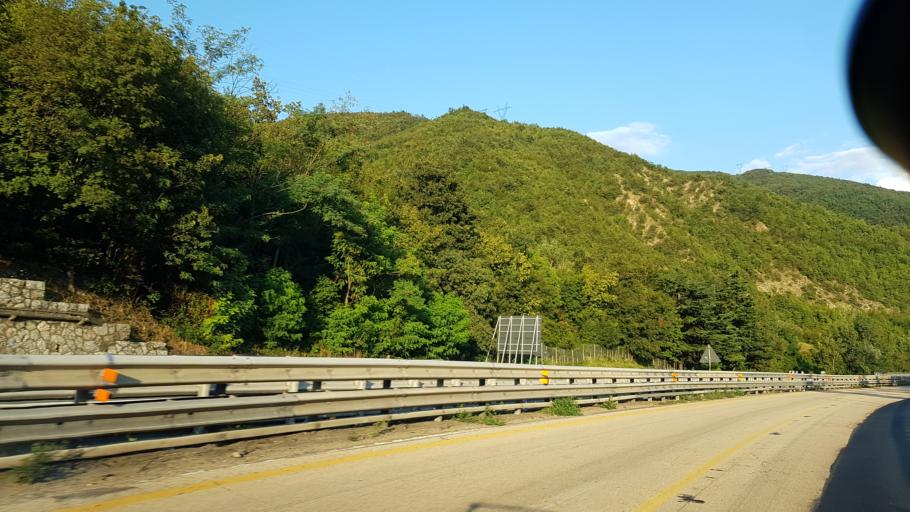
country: IT
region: Liguria
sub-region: Provincia di Genova
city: Isola del Cantone
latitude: 44.6643
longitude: 8.9479
